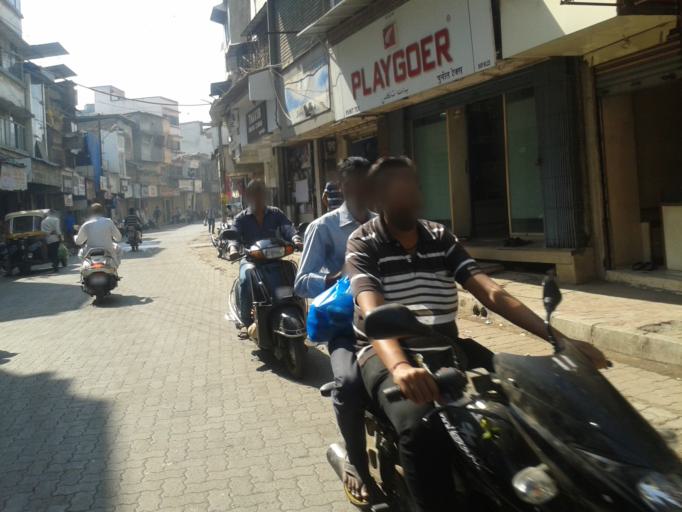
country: IN
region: Maharashtra
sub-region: Thane
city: Ulhasnagar
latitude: 19.2373
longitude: 73.1648
